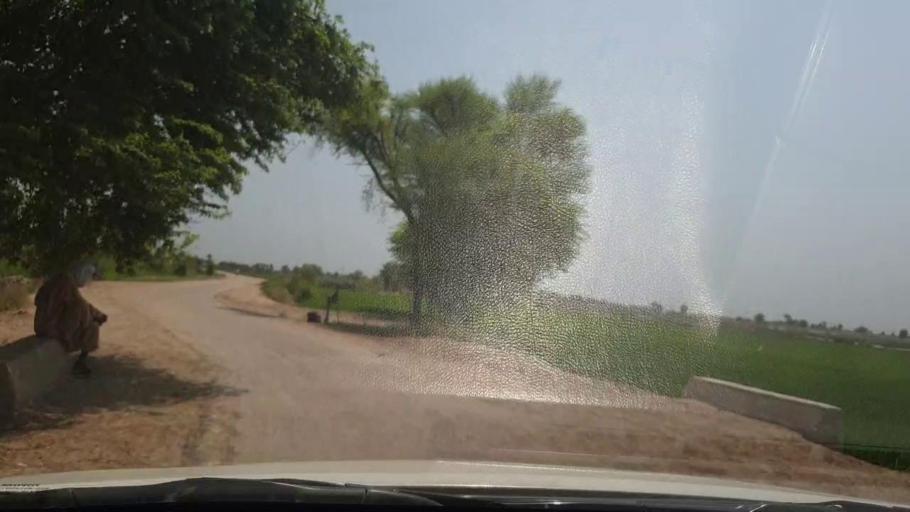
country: PK
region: Sindh
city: Rustam jo Goth
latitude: 28.0296
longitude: 68.7985
